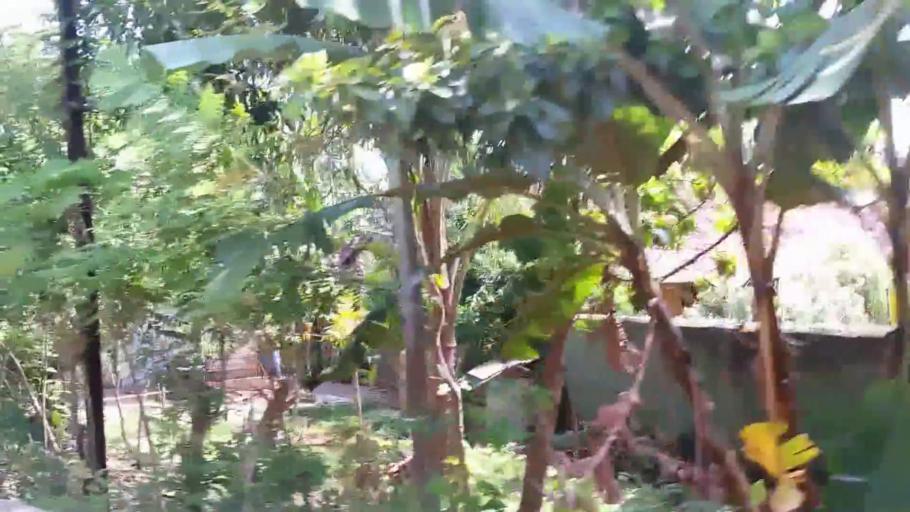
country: LK
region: Southern
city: Hikkaduwa
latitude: 6.1702
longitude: 80.0878
